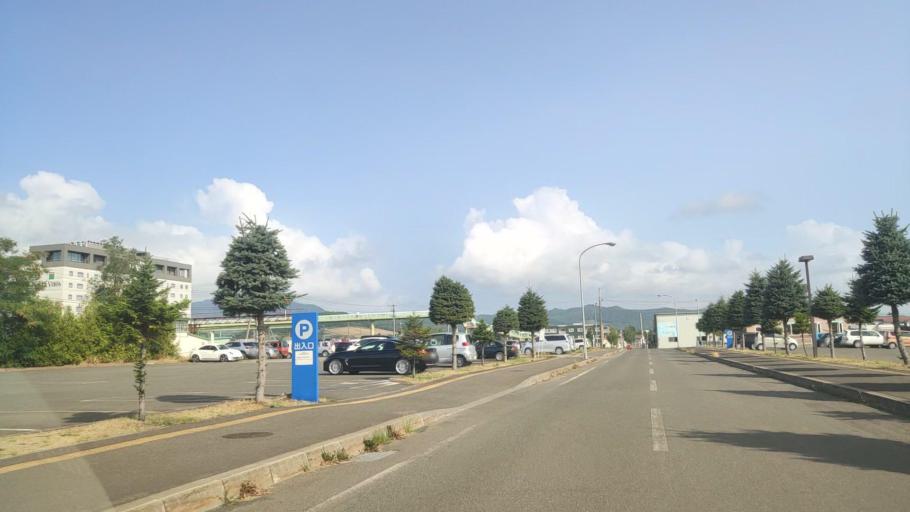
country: JP
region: Hokkaido
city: Shimo-furano
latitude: 43.3482
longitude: 142.3918
